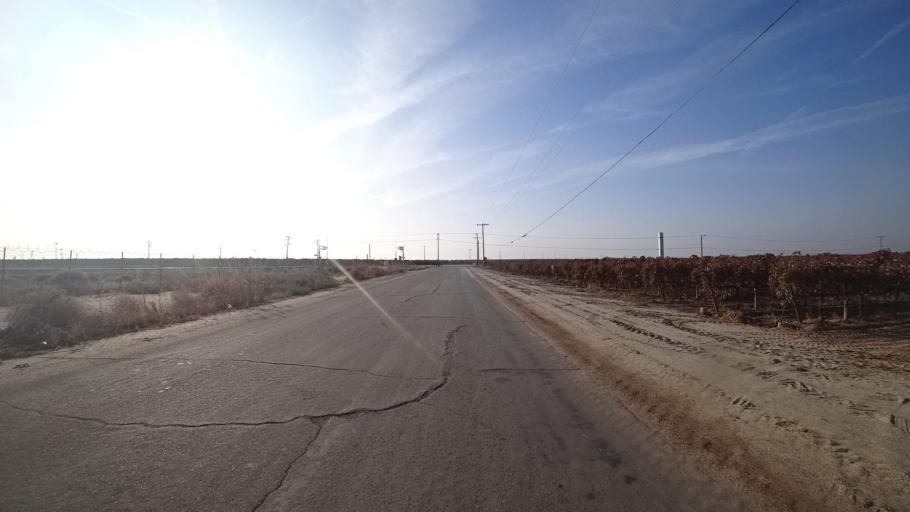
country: US
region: California
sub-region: Kern County
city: McFarland
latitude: 35.6758
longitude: -119.1872
